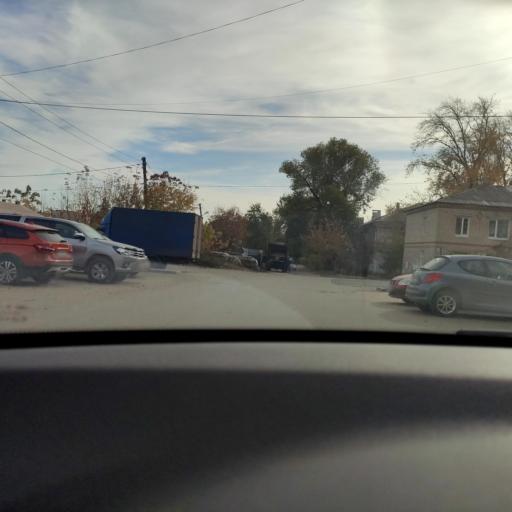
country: RU
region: Samara
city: Samara
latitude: 53.2044
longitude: 50.1939
